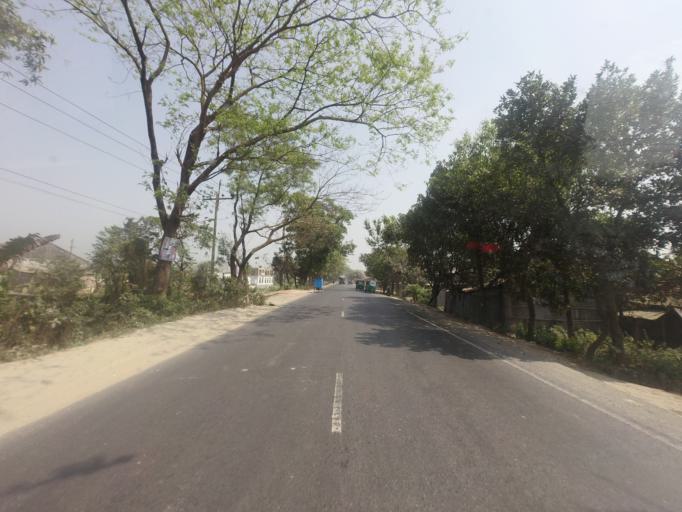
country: BD
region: Dhaka
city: Bhairab Bazar
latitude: 24.0406
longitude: 91.0388
